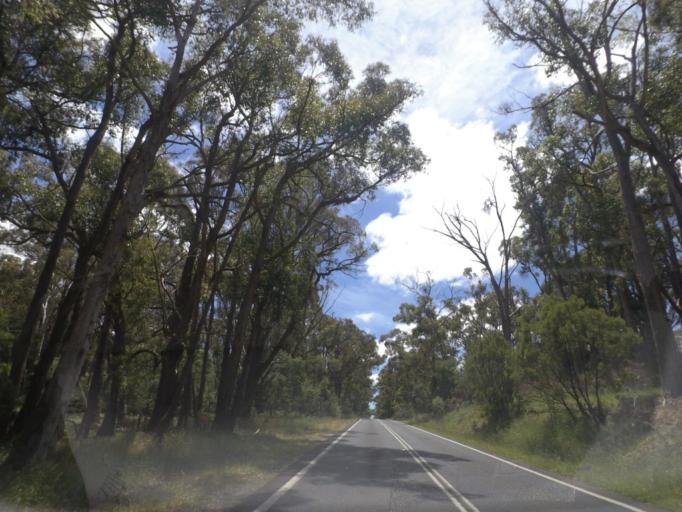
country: AU
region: Victoria
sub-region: Mount Alexander
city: Castlemaine
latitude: -37.3110
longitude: 144.1658
